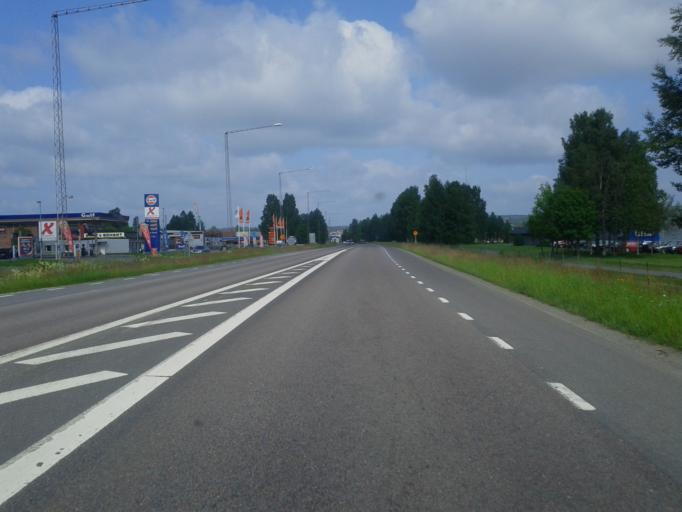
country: SE
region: Vaesterbotten
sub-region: Skelleftea Kommun
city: Skelleftea
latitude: 64.7381
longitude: 20.9653
